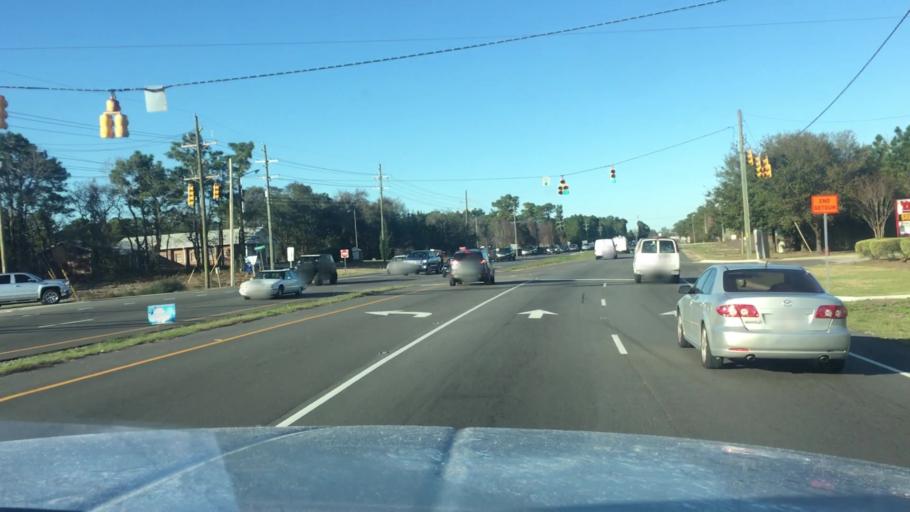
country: US
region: North Carolina
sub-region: New Hanover County
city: Myrtle Grove
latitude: 34.1256
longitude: -77.8996
